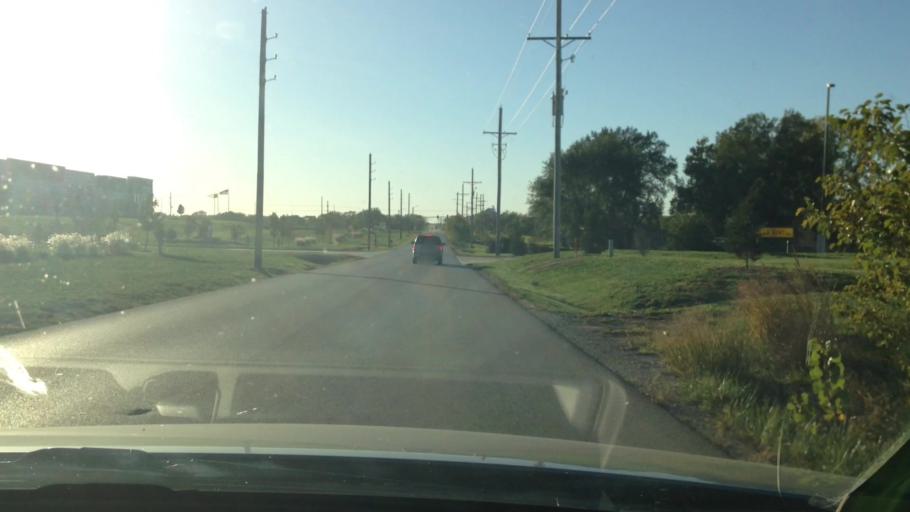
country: US
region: Kansas
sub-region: Johnson County
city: Gardner
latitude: 38.7820
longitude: -94.9411
